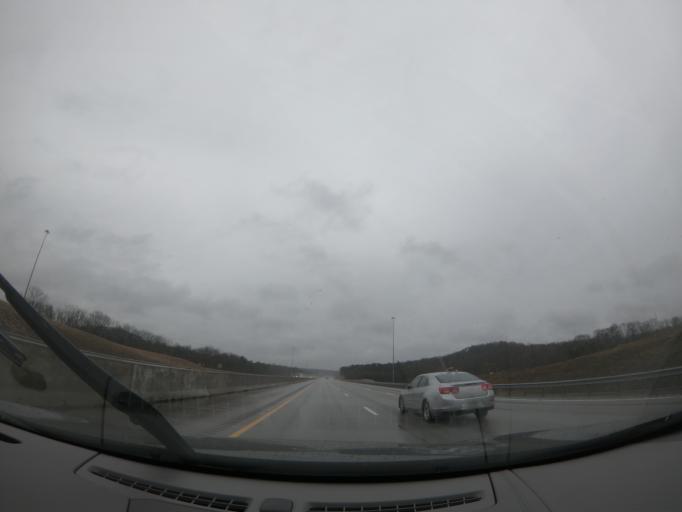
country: US
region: Kentucky
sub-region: Hart County
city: Horse Cave
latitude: 37.2012
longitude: -85.9377
